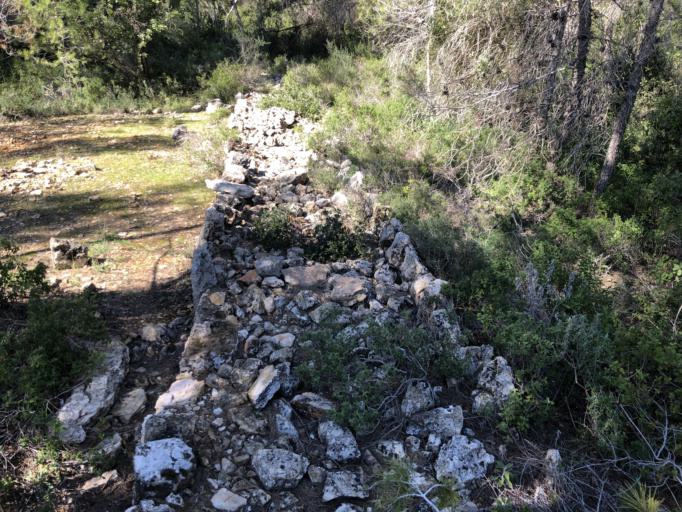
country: IL
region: Jerusalem
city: Bet Shemesh
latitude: 31.7465
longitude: 35.0461
